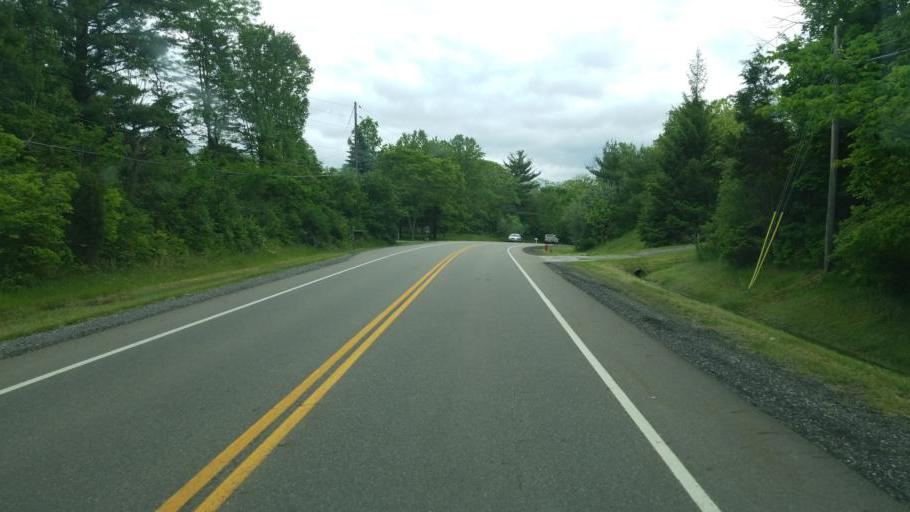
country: US
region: Ohio
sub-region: Summit County
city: Richfield
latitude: 41.2398
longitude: -81.6274
